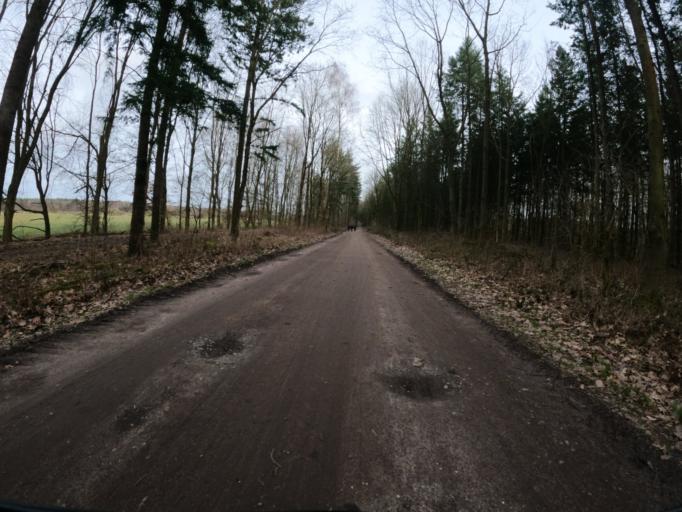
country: DE
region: Schleswig-Holstein
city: Appen
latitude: 53.6121
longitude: 9.7559
